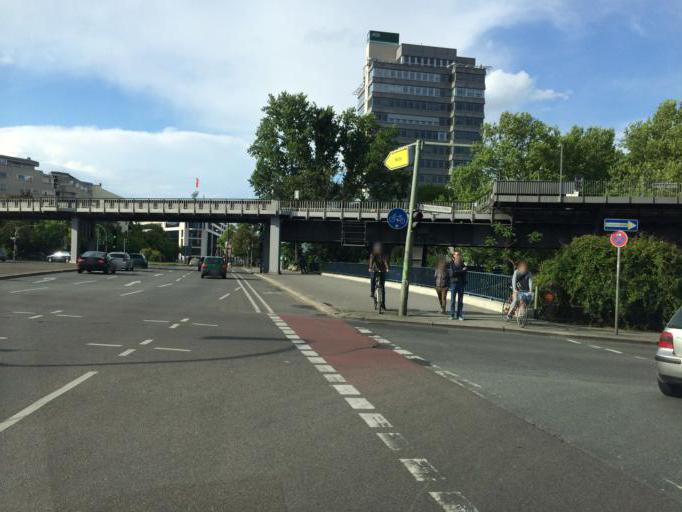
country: DE
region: Berlin
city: Bezirk Kreuzberg
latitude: 52.4974
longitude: 13.3893
